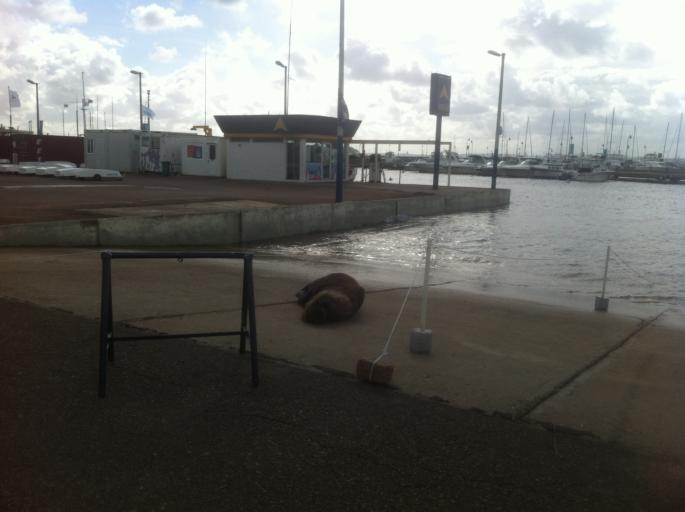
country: UY
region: Maldonado
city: Punta del Este
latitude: -34.9647
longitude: -54.9483
